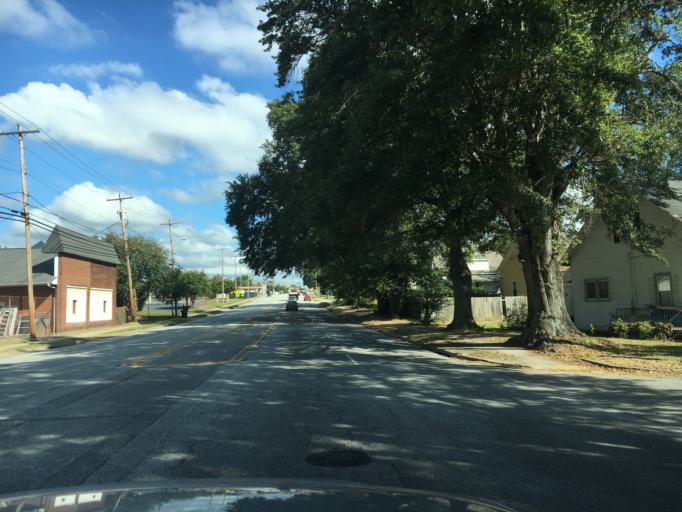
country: US
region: South Carolina
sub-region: Greenville County
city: Greer
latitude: 34.9326
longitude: -82.2225
